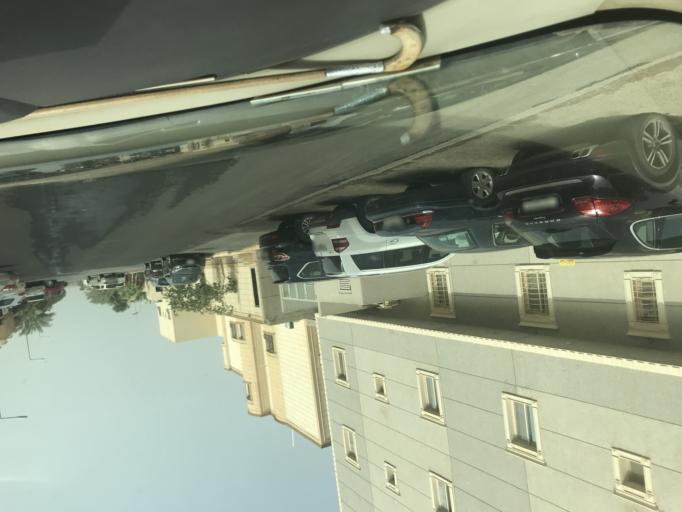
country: SA
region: Ar Riyad
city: Riyadh
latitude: 24.7997
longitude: 46.6666
